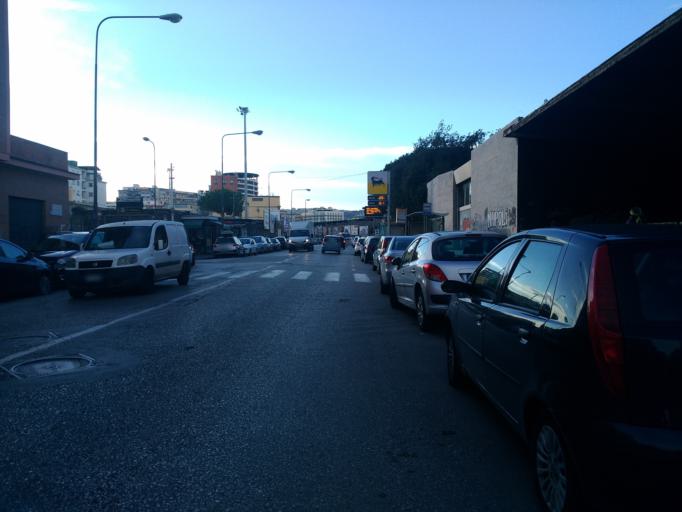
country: IT
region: Campania
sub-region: Provincia di Napoli
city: Napoli
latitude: 40.8500
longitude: 14.2791
